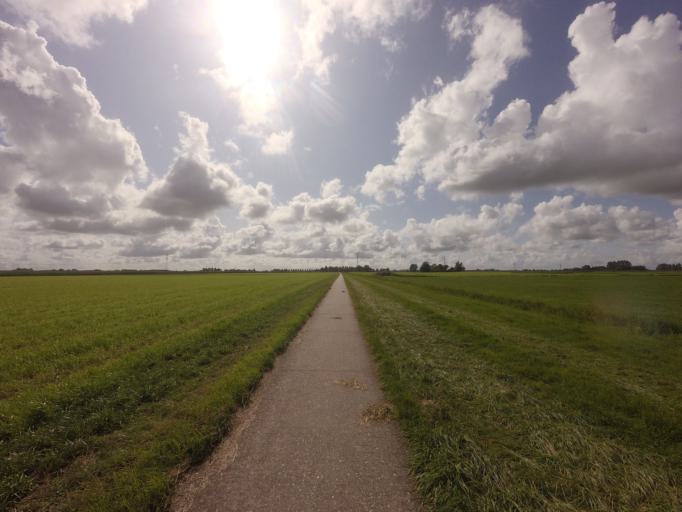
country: NL
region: Friesland
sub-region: Sudwest Fryslan
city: Sneek
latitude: 53.0665
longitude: 5.6384
